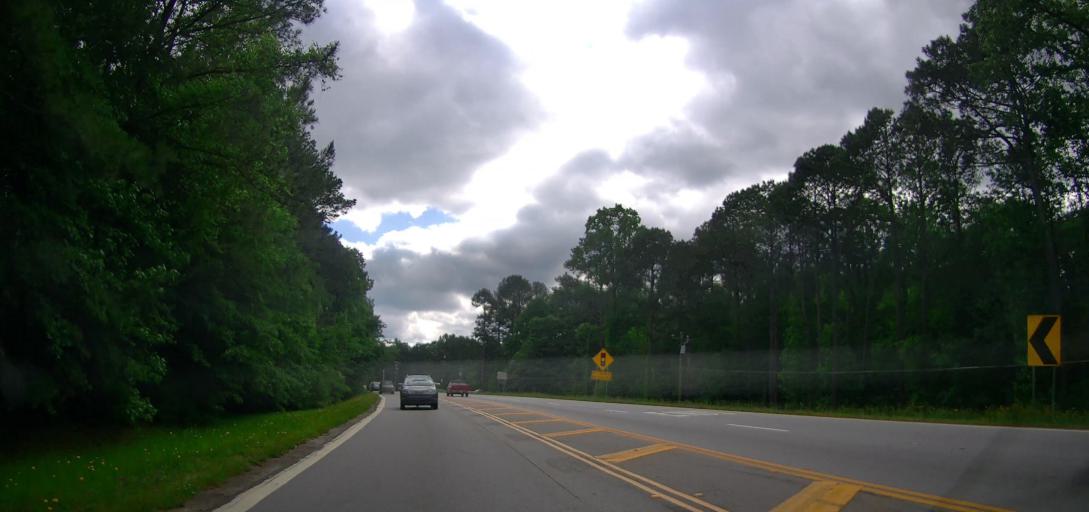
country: US
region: Georgia
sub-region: Walton County
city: Walnut Grove
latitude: 33.7205
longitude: -83.9239
